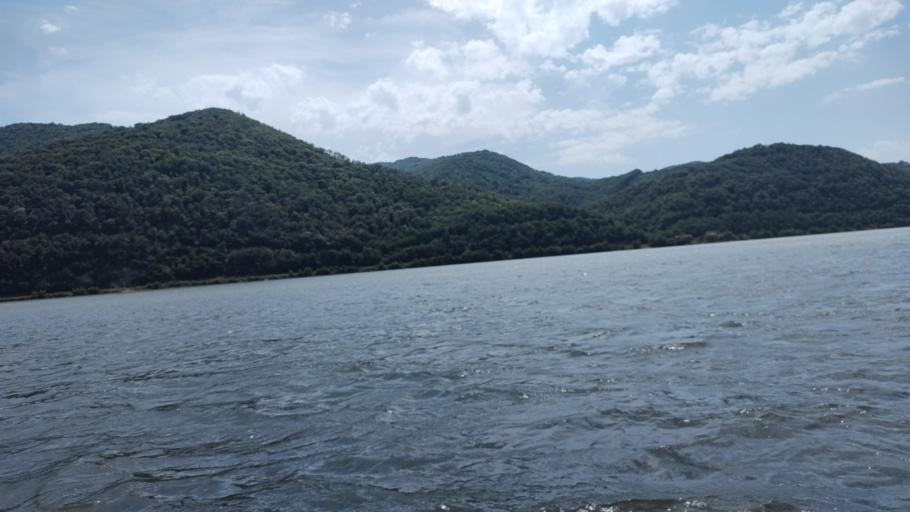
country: RO
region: Caras-Severin
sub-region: Comuna Berzasca
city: Liubcova
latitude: 44.6488
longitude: 21.8887
